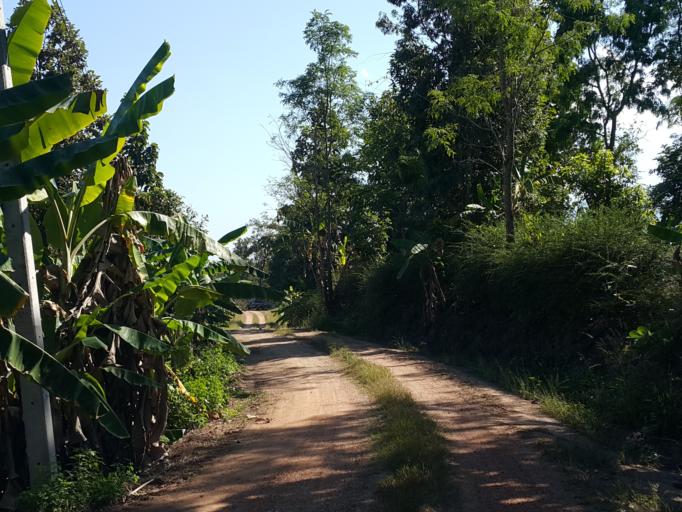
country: TH
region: Chiang Mai
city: Mae Taeng
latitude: 18.9551
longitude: 98.9018
